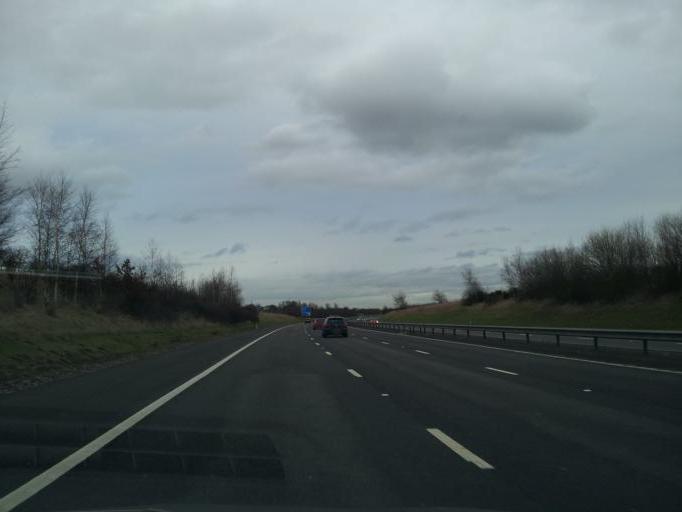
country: GB
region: England
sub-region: Staffordshire
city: Shenstone
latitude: 52.6530
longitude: -1.8732
